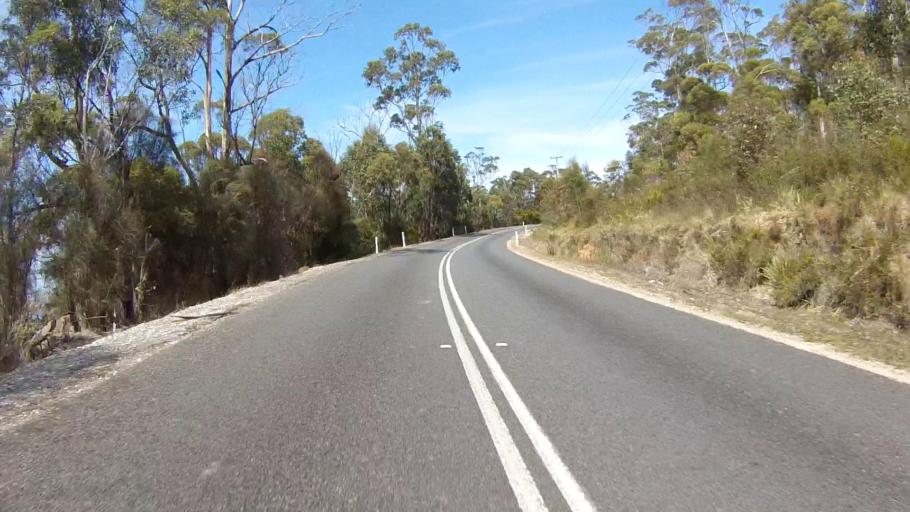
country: AU
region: Tasmania
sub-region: Huon Valley
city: Cygnet
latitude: -43.2805
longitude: 147.1742
